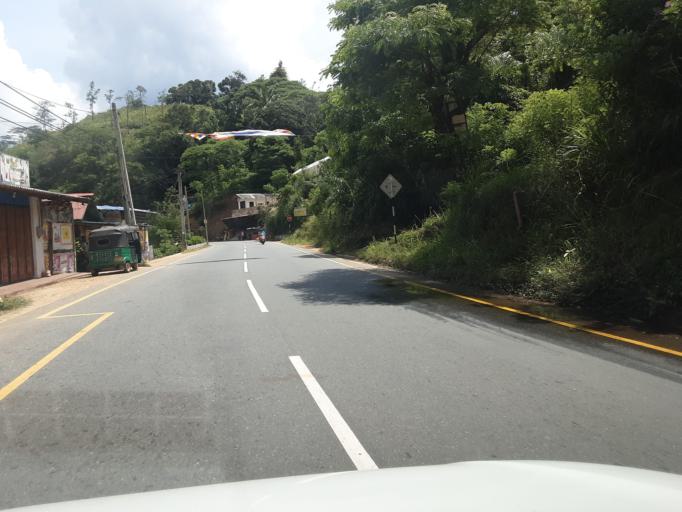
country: LK
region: Central
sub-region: Nuwara Eliya District
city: Nuwara Eliya
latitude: 6.9158
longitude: 80.9058
